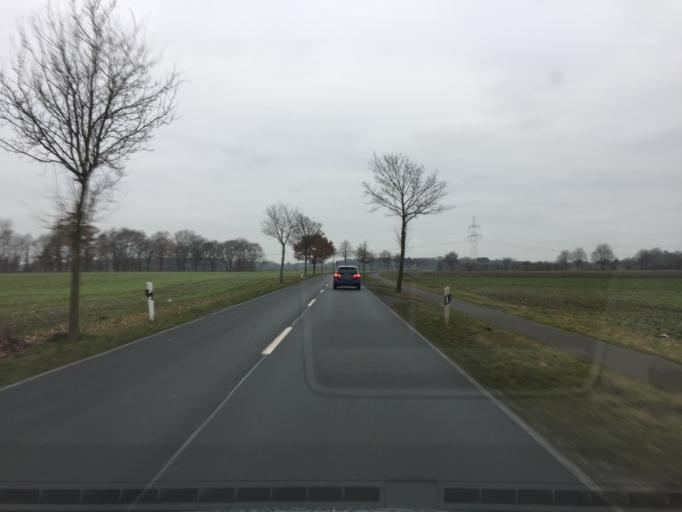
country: DE
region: Lower Saxony
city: Langwedel
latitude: 53.0184
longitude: 9.1680
